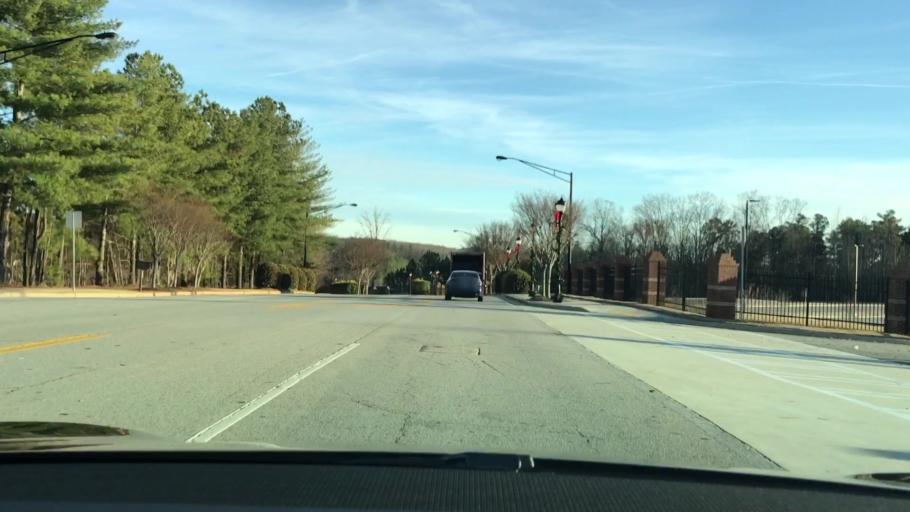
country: US
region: Georgia
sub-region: Gwinnett County
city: Buford
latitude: 34.1292
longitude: -83.9861
